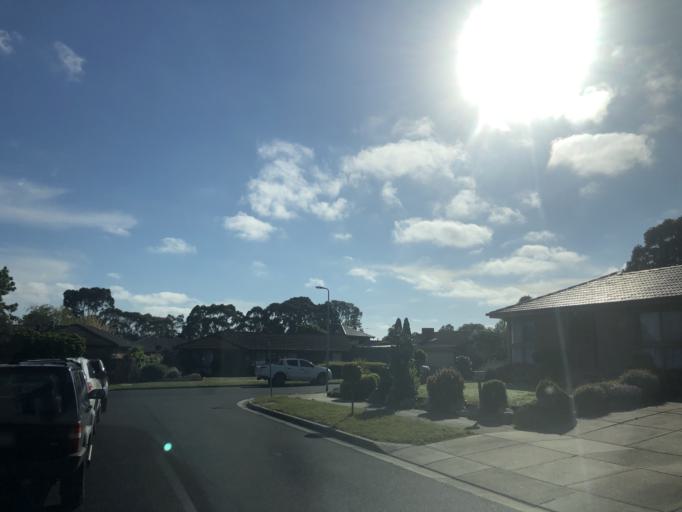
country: AU
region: Victoria
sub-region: Casey
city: Hallam
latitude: -37.9982
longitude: 145.2690
